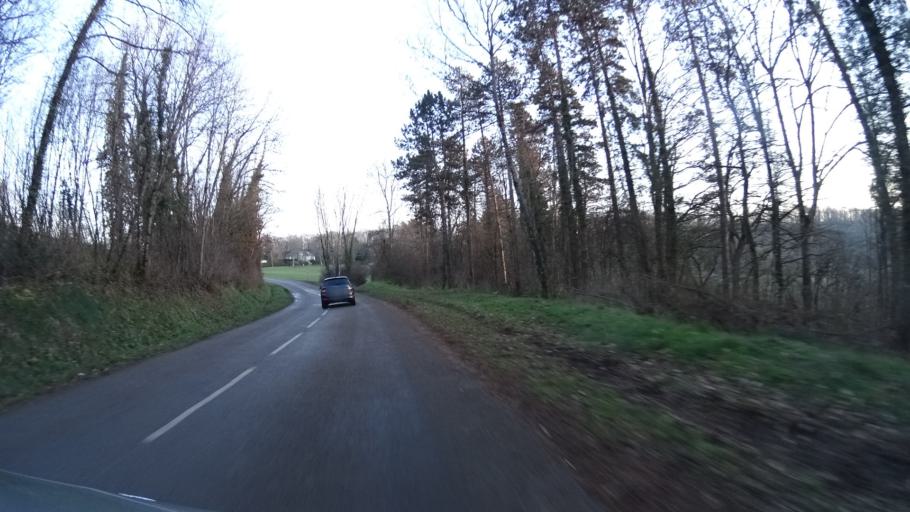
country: FR
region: Franche-Comte
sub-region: Departement du Doubs
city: Morre
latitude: 47.2158
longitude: 6.0545
